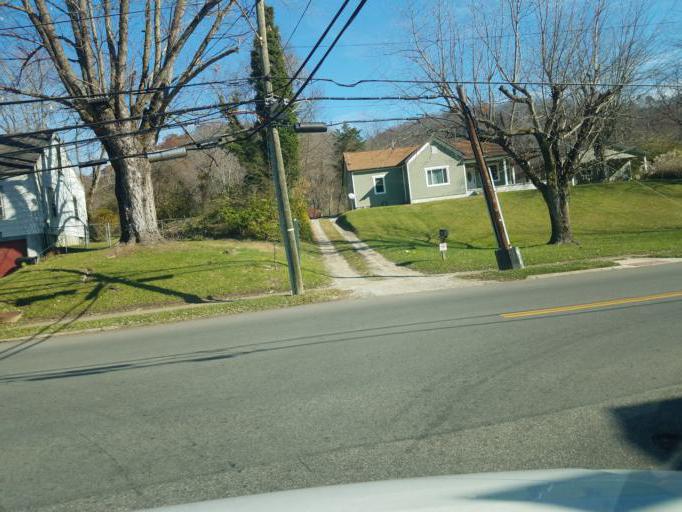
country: US
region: Ohio
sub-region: Scioto County
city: New Boston
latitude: 38.7629
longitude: -82.9353
